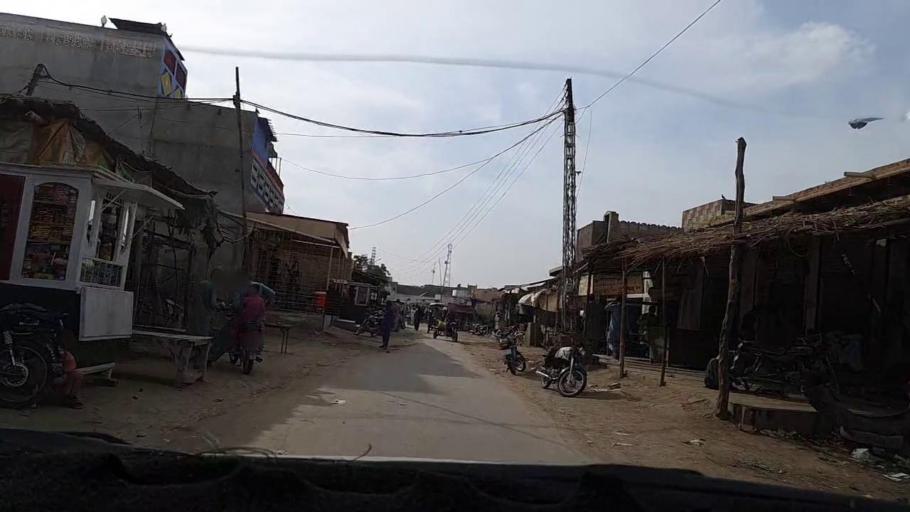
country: PK
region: Sindh
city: Pithoro
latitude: 25.5187
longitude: 69.2356
